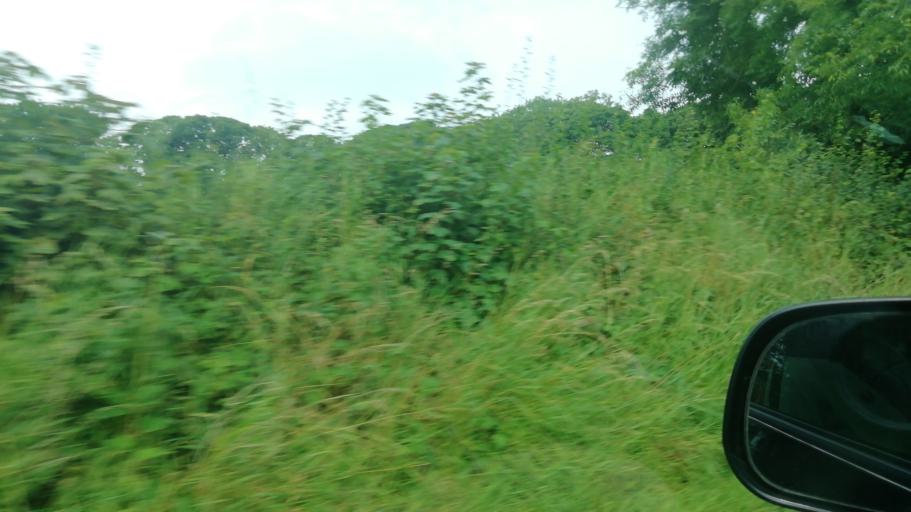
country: IE
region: Munster
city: Fethard
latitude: 52.5767
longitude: -7.5852
